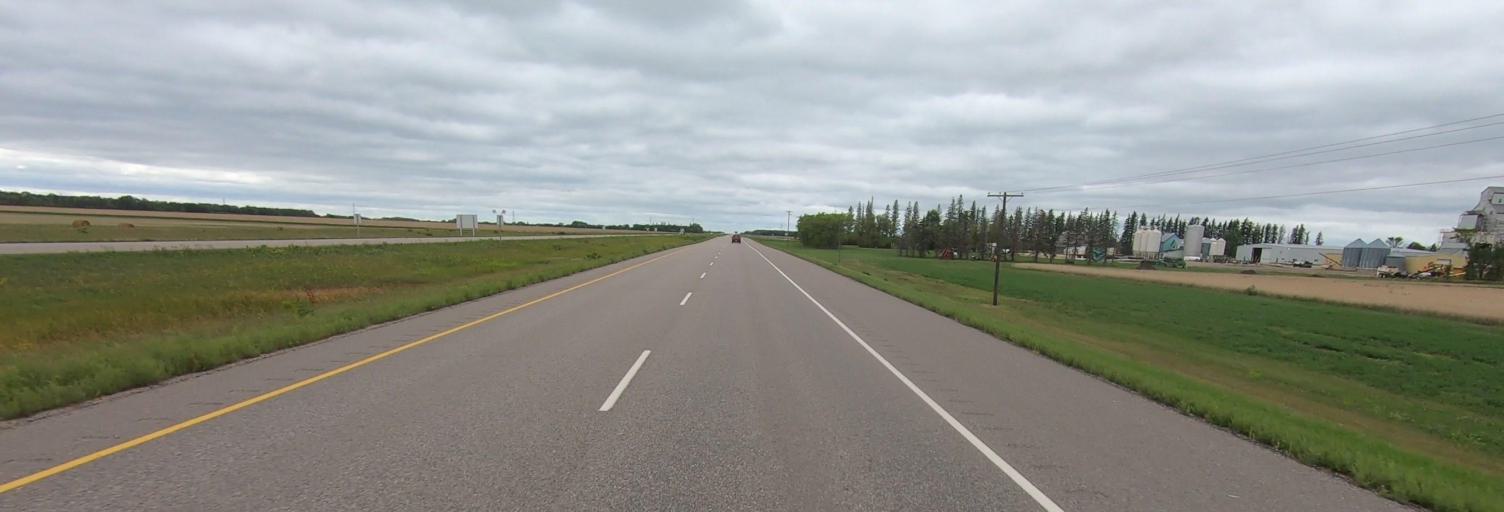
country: CA
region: Manitoba
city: Portage la Prairie
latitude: 49.9752
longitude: -98.5090
